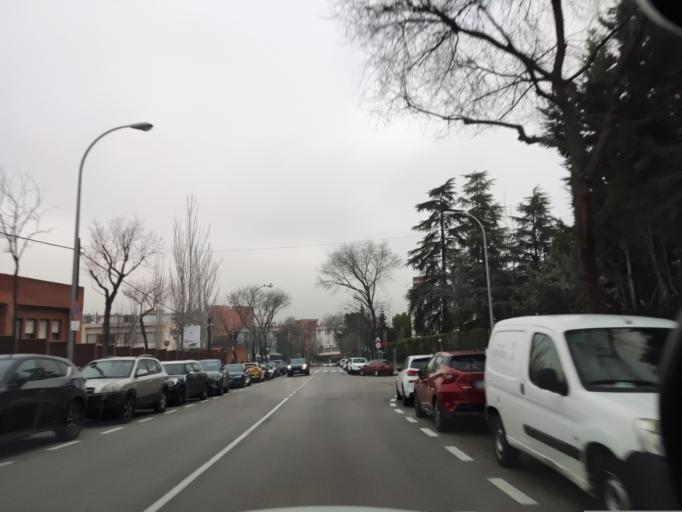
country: ES
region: Madrid
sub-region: Provincia de Madrid
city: Fuencarral-El Pardo
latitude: 40.4885
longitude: -3.7139
